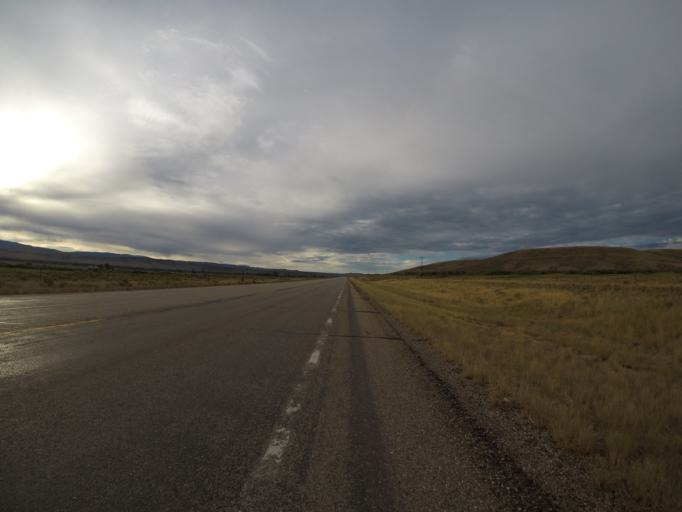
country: US
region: Wyoming
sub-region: Carbon County
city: Saratoga
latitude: 41.3901
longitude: -106.7572
